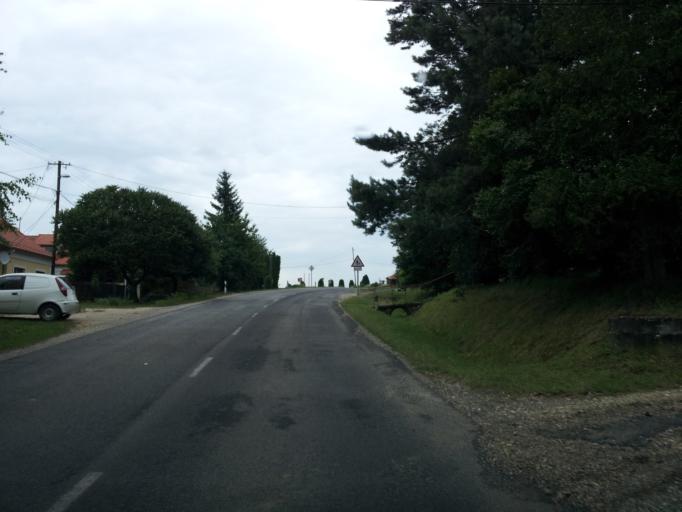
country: HU
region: Vas
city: Kormend
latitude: 46.9742
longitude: 16.6321
